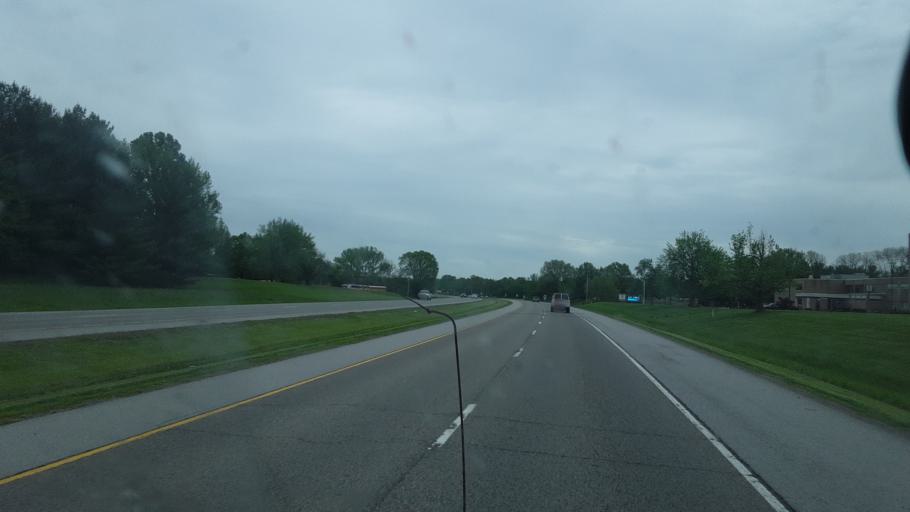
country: US
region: Illinois
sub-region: Jackson County
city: Carbondale
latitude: 37.7365
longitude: -89.2523
